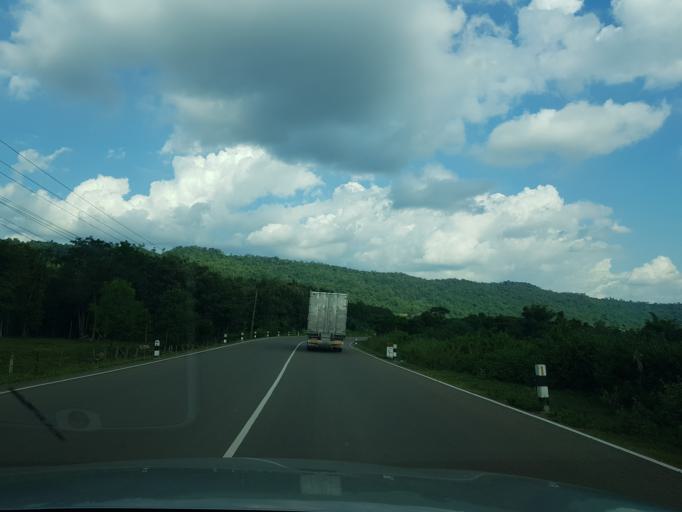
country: TH
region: Nong Khai
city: Sangkhom
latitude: 18.0246
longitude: 102.3805
